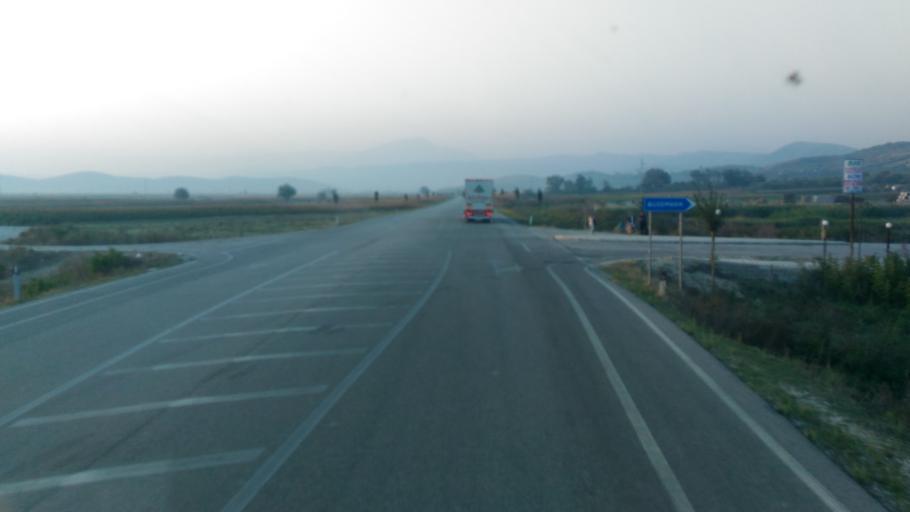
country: AL
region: Fier
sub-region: Rrethi i Fierit
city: Cakran
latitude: 40.5800
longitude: 19.6203
